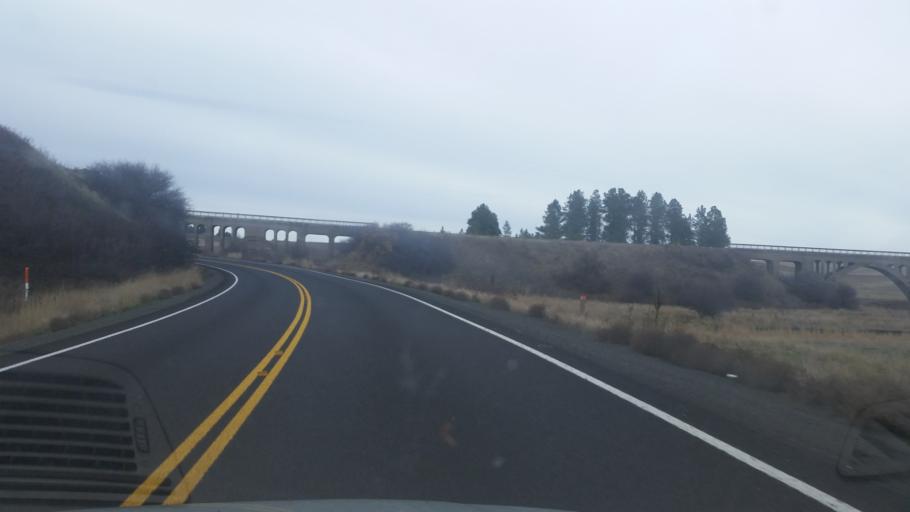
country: US
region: Washington
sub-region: Whitman County
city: Colfax
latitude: 47.2202
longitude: -117.3621
